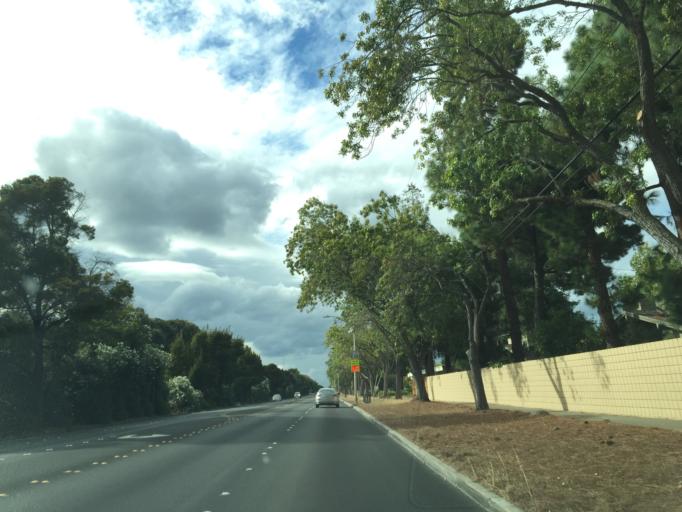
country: US
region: California
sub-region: Santa Clara County
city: Los Altos
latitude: 37.4103
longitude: -122.1112
